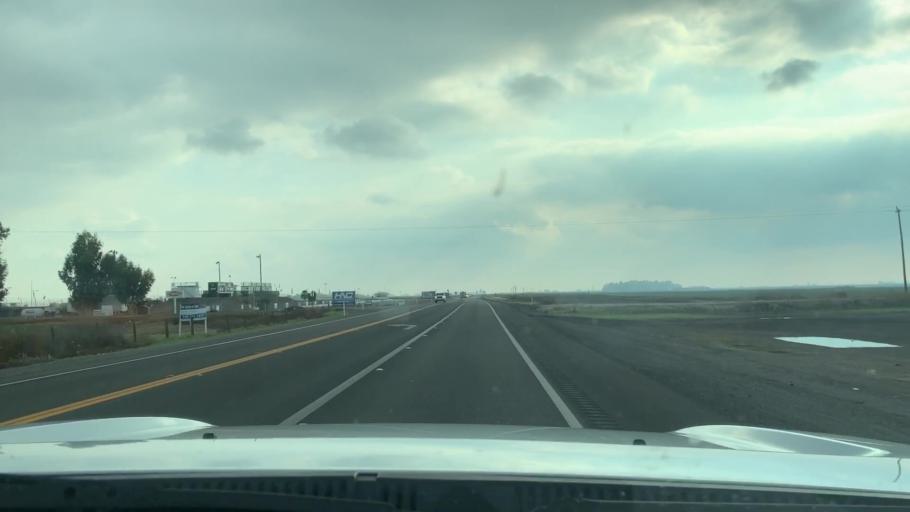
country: US
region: California
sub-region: Kings County
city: Lemoore
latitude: 36.2701
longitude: -119.8078
